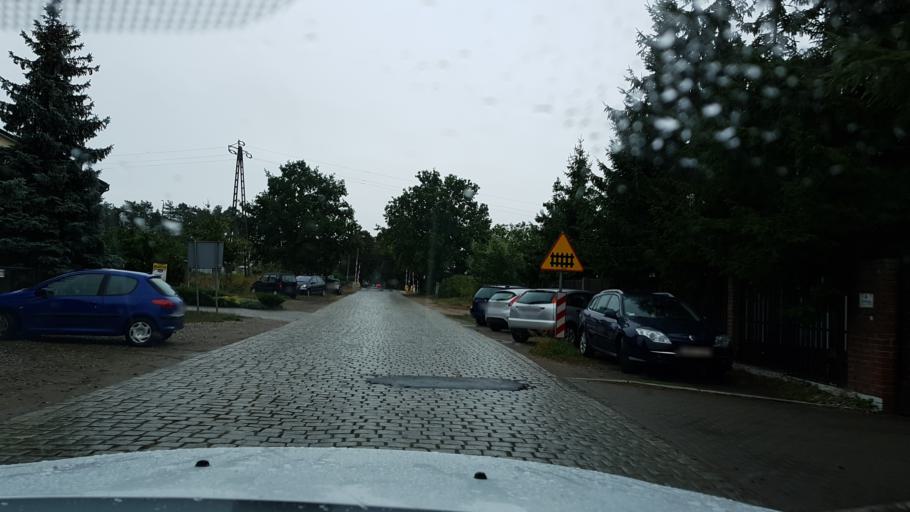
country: PL
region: West Pomeranian Voivodeship
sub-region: Powiat gryfinski
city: Gryfino
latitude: 53.2229
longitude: 14.4868
